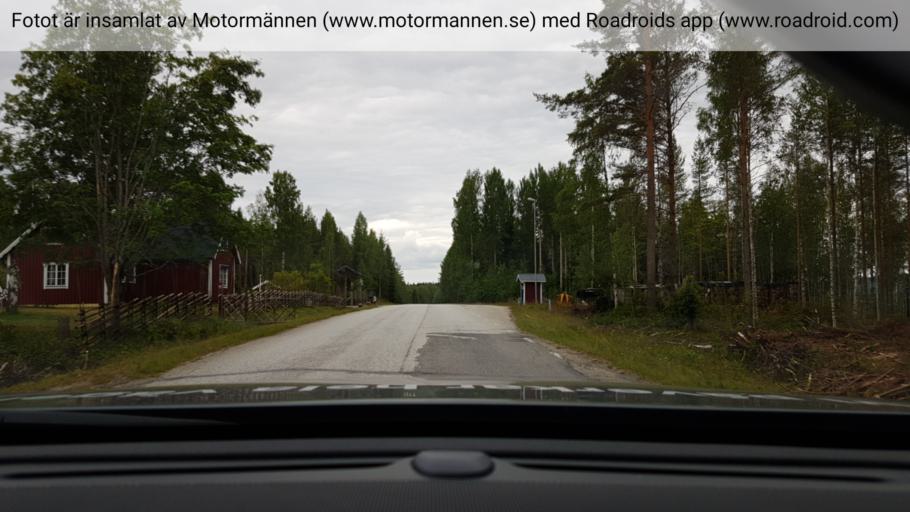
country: SE
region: Vaesterbotten
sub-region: Vannas Kommun
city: Vannasby
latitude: 64.0009
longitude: 19.9170
